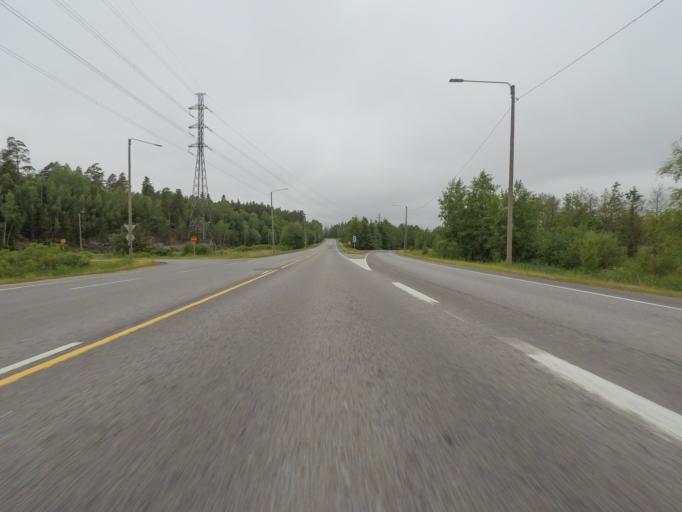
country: FI
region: Varsinais-Suomi
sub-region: Turku
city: Raisio
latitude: 60.4648
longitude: 22.1367
